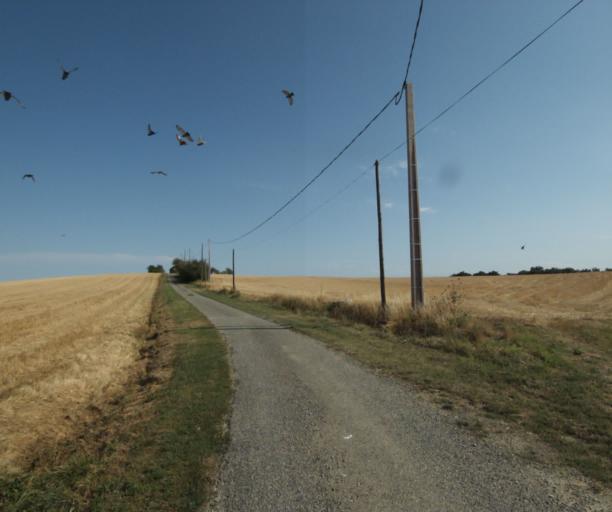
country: FR
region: Midi-Pyrenees
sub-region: Departement de la Haute-Garonne
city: Avignonet-Lauragais
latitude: 43.4176
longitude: 1.8165
